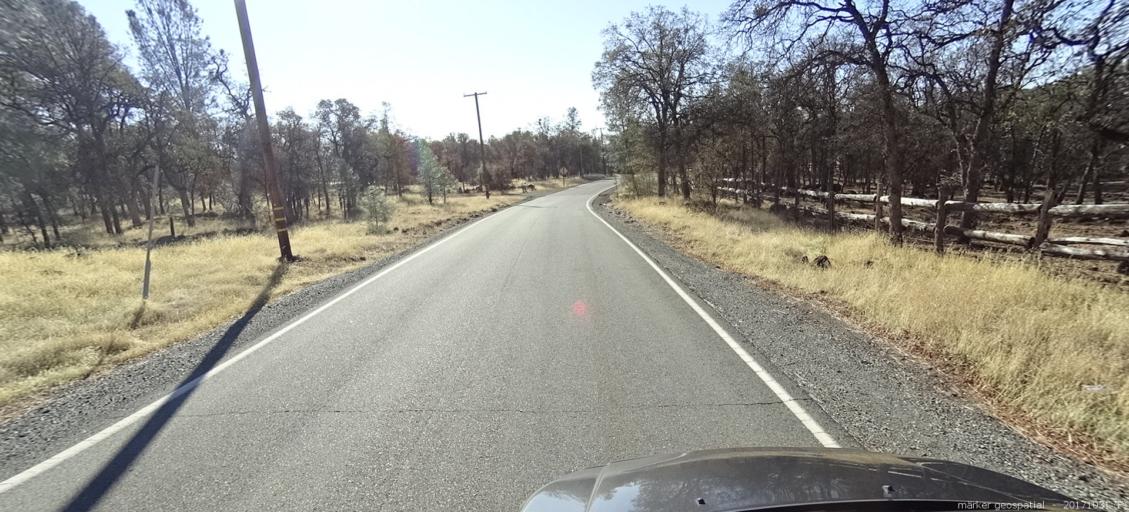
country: US
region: California
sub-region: Shasta County
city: Shingletown
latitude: 40.4553
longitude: -121.8994
